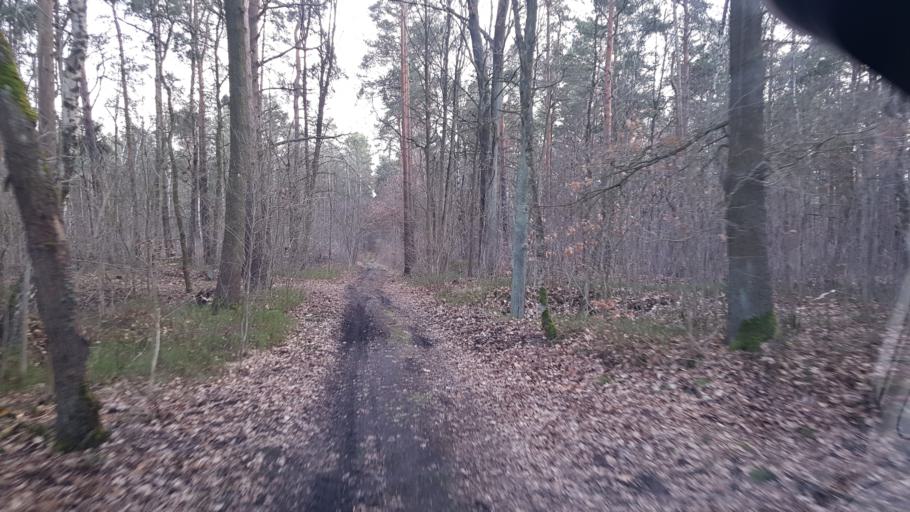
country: DE
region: Brandenburg
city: Schonborn
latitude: 51.5927
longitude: 13.4861
